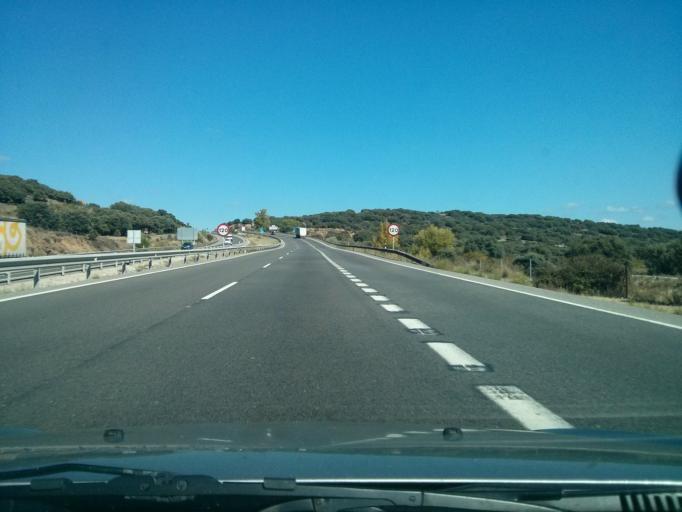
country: ES
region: Madrid
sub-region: Provincia de Madrid
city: Buitrago del Lozoya
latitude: 40.9497
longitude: -3.6394
